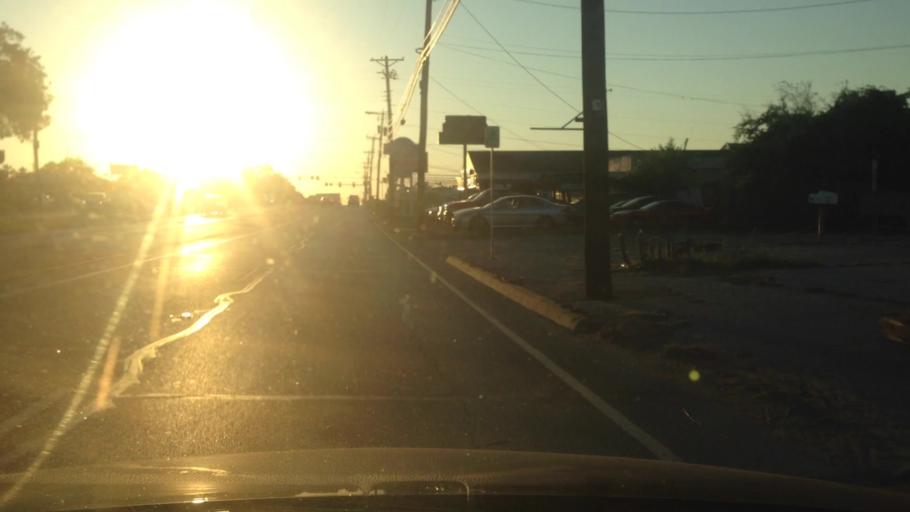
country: US
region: Texas
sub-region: Tarrant County
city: Haltom City
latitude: 32.7951
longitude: -97.2931
